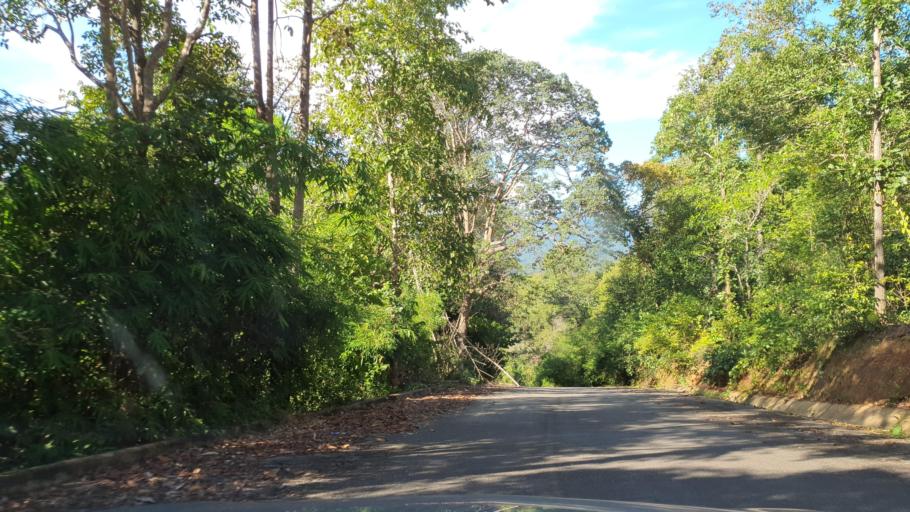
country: TH
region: Chiang Mai
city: Mae On
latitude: 18.7735
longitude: 99.2887
